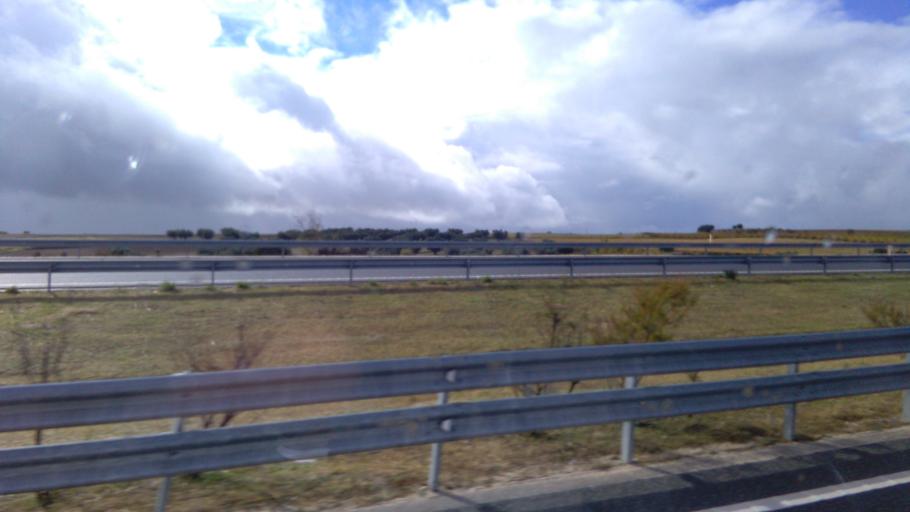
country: ES
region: Madrid
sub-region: Provincia de Madrid
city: El Alamo
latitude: 40.2595
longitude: -3.9858
